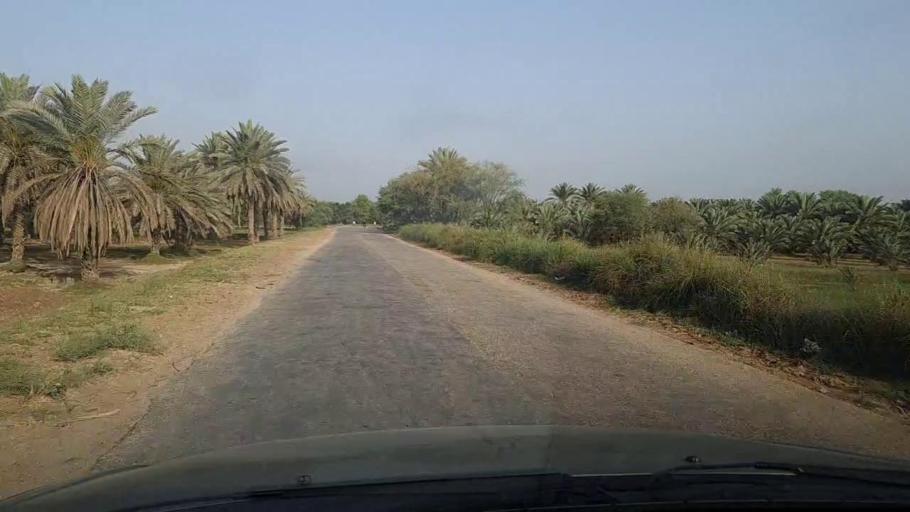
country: PK
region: Sindh
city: Pir jo Goth
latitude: 27.5617
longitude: 68.6609
